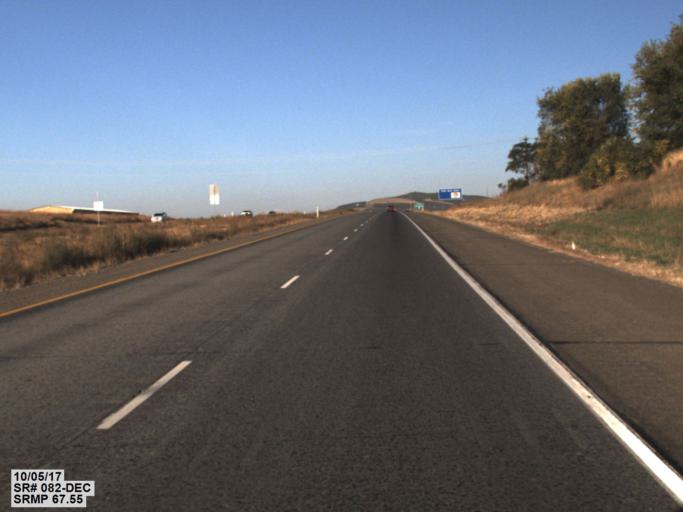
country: US
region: Washington
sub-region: Yakima County
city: Sunnyside
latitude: 46.3062
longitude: -120.0075
